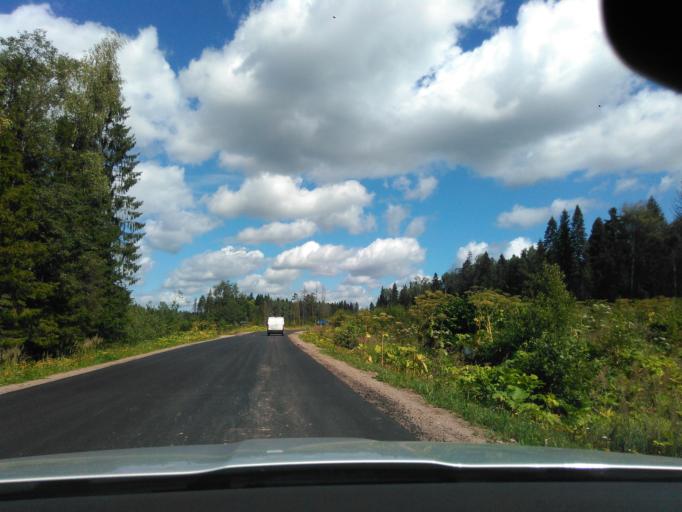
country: RU
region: Moskovskaya
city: Klin
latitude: 56.2531
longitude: 36.8363
